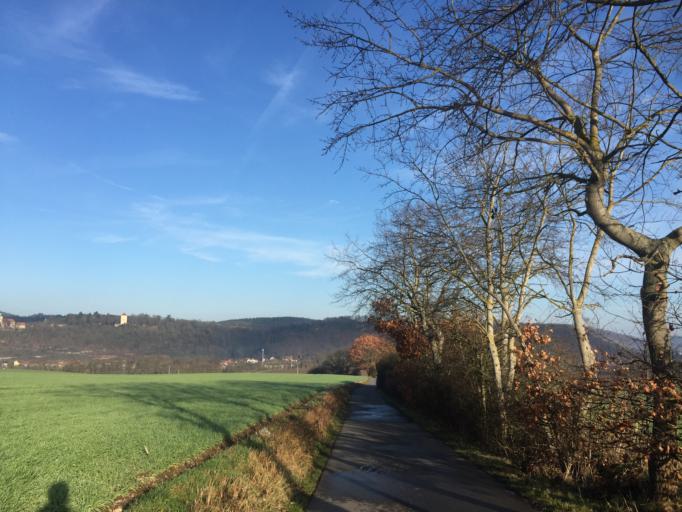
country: DE
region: Thuringia
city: Orlamunde
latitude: 50.7647
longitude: 11.5312
